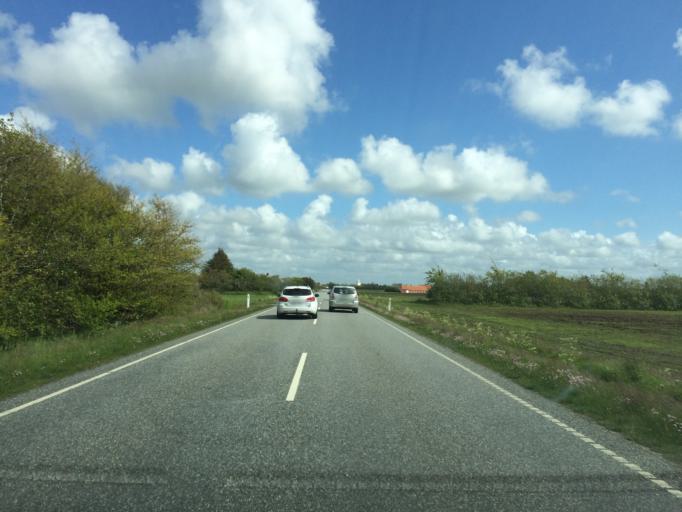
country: DK
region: Central Jutland
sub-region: Holstebro Kommune
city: Ulfborg
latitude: 56.3142
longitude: 8.1686
